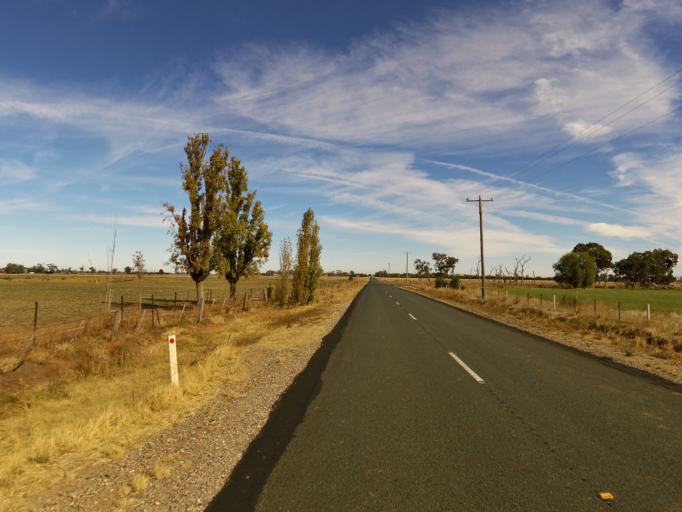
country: AU
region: Victoria
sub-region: Campaspe
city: Echuca
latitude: -36.2991
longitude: 144.4833
